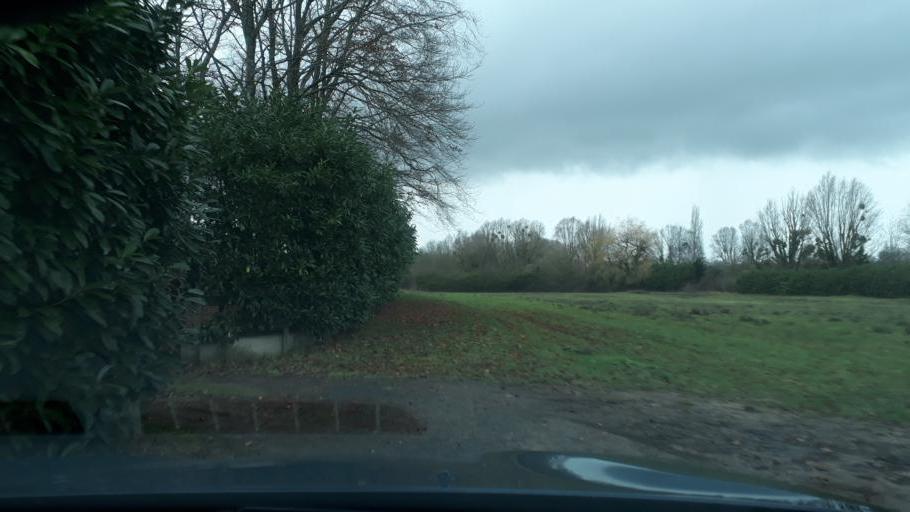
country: FR
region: Centre
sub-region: Departement du Loiret
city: Lailly-en-Val
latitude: 47.7779
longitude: 1.6987
